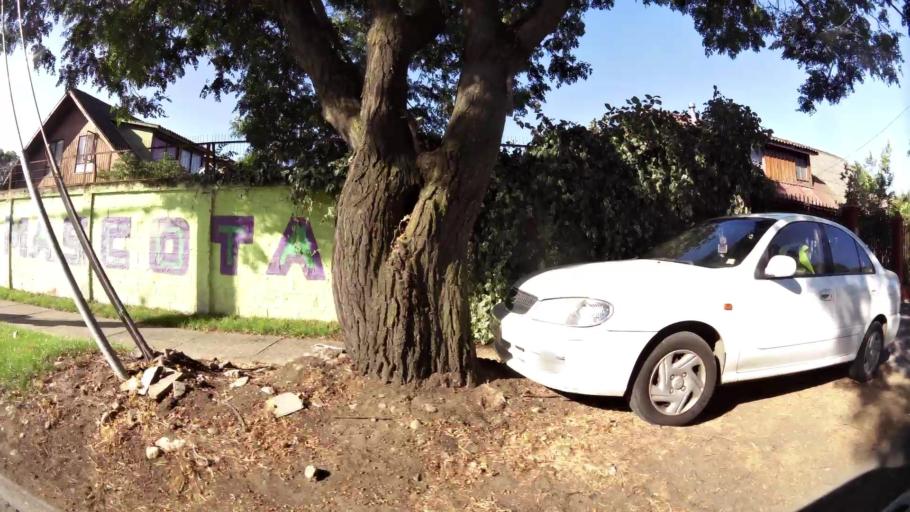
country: CL
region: Maule
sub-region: Provincia de Talca
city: Talca
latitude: -35.4416
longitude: -71.6749
